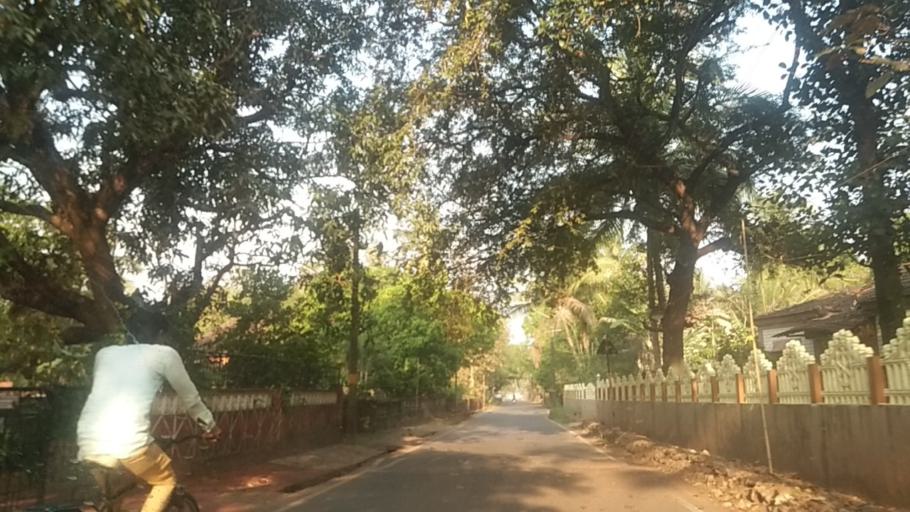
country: IN
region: Goa
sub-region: South Goa
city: Chinchinim
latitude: 15.2364
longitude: 73.9827
